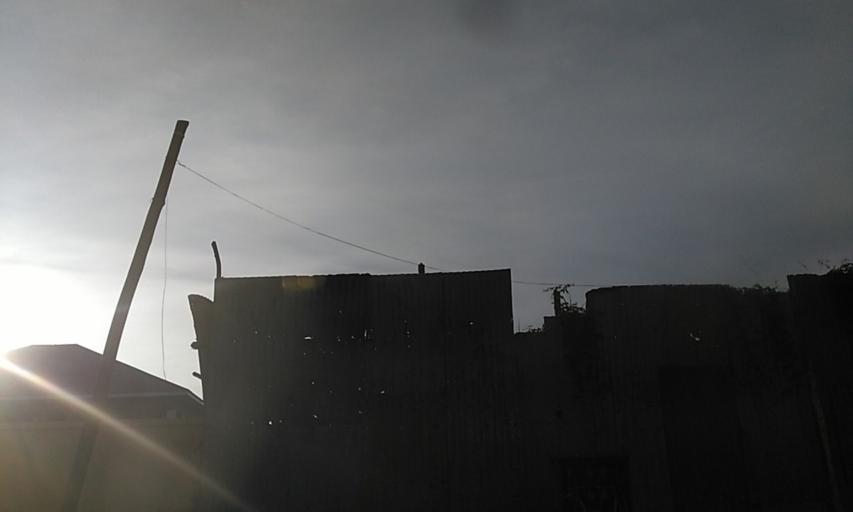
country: UG
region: Central Region
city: Kampala Central Division
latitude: 0.3213
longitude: 32.5729
